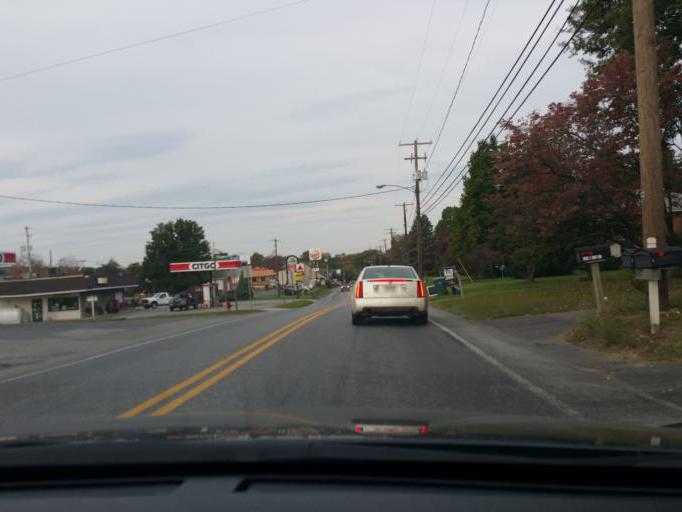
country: US
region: Pennsylvania
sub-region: Lancaster County
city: Quarryville
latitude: 39.8953
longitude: -76.1732
